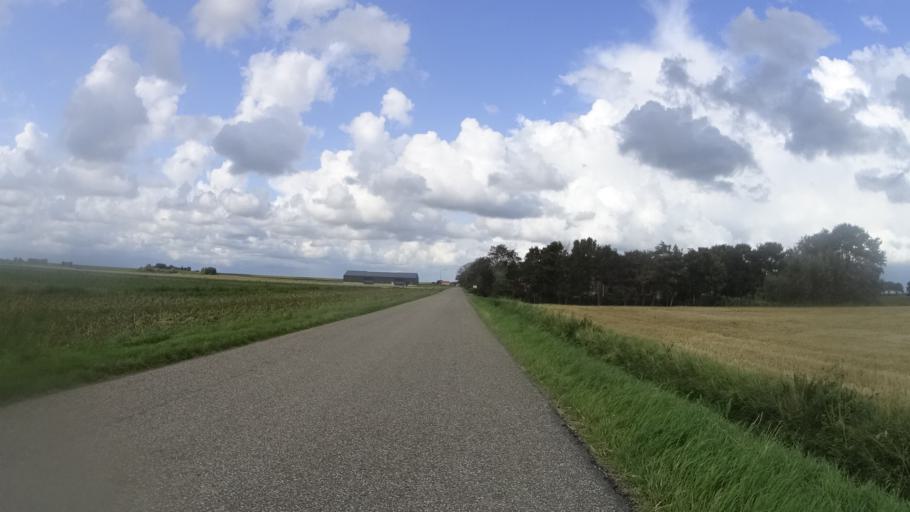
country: NL
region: North Holland
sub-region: Gemeente Schagen
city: Schagen
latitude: 52.8655
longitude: 4.8961
